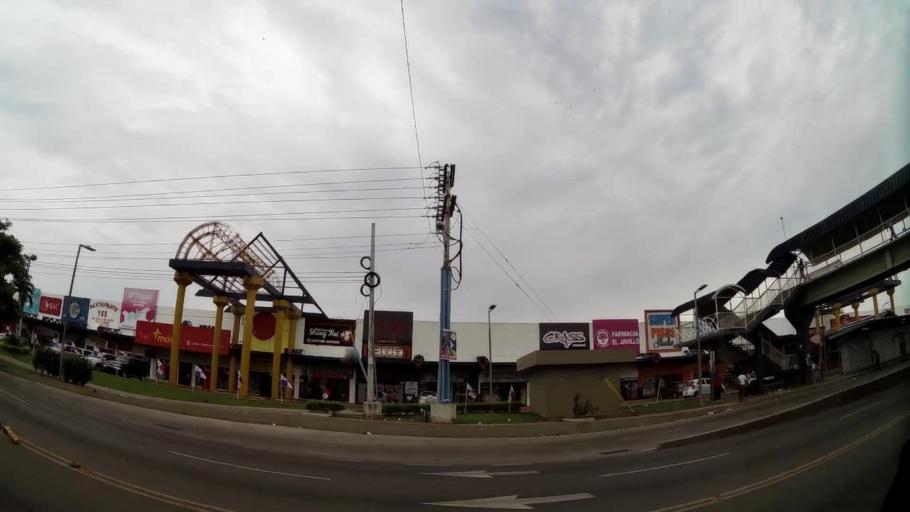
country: PA
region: Panama
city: San Miguelito
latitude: 9.0454
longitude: -79.4499
